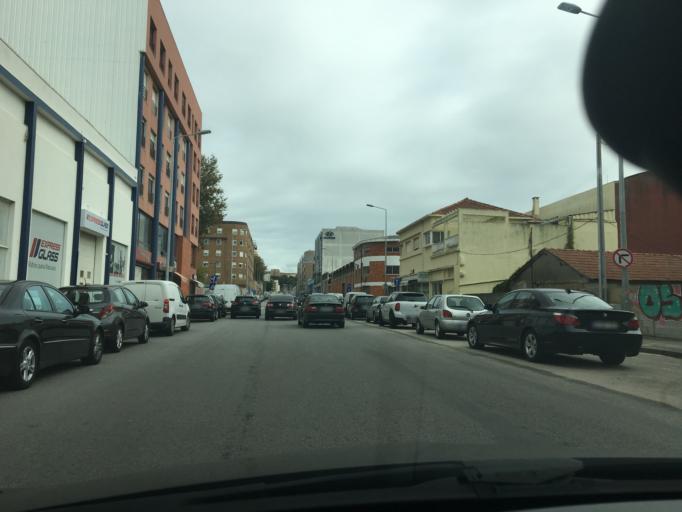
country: PT
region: Porto
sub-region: Matosinhos
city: Matosinhos
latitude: 41.1769
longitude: -8.6860
